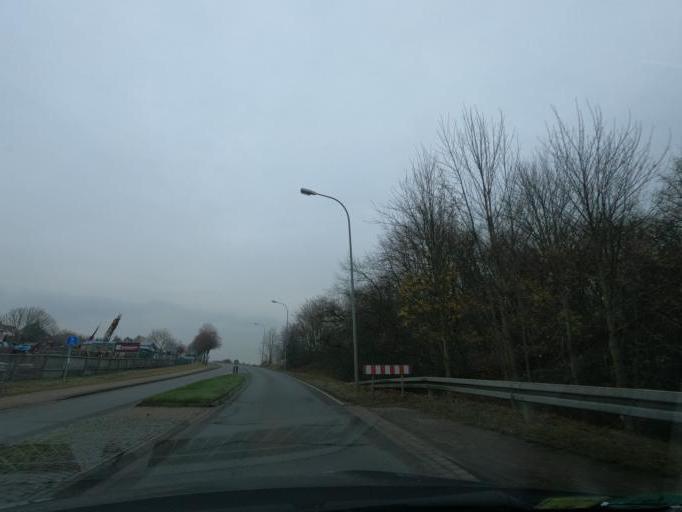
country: DE
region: Lower Saxony
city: Wolfenbuettel
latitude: 52.1521
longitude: 10.5678
